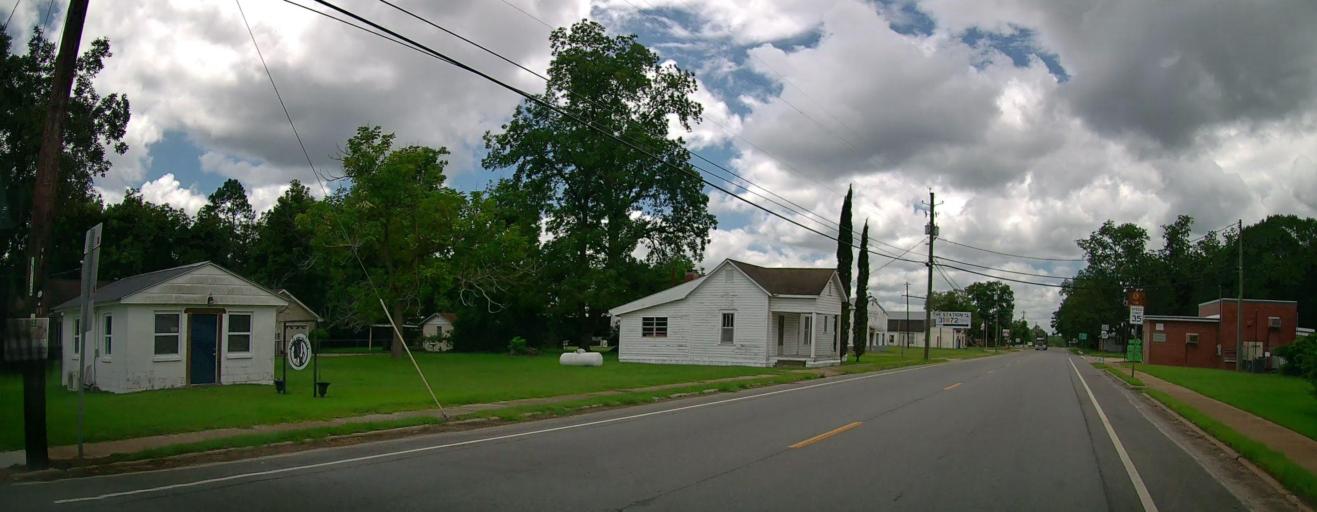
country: US
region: Georgia
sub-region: Wilcox County
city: Rochelle
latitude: 31.9449
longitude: -83.5409
